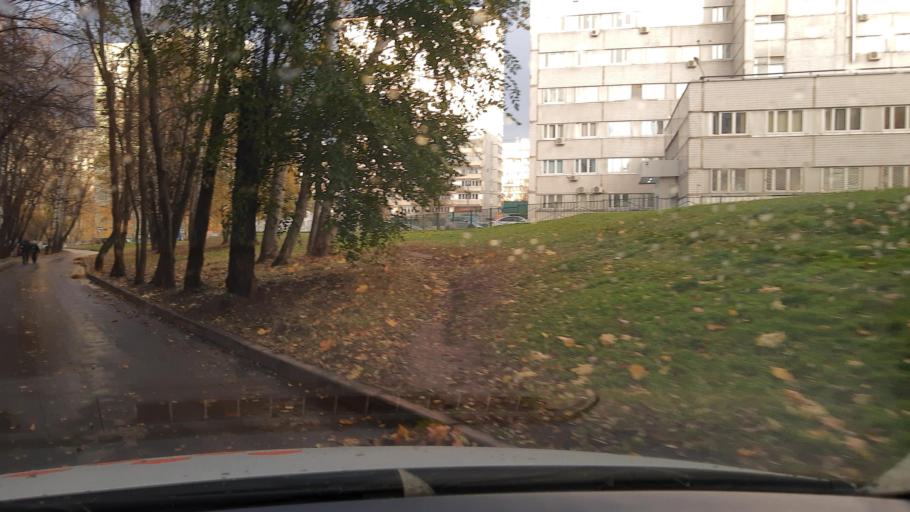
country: RU
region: Moscow
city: Orekhovo-Borisovo
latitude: 55.6072
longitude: 37.7313
